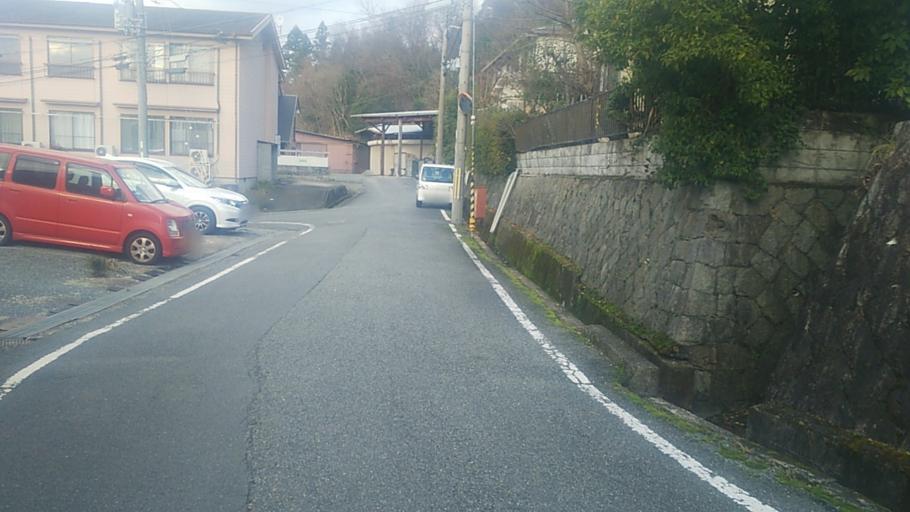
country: JP
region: Kyoto
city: Kameoka
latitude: 34.9984
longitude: 135.5563
